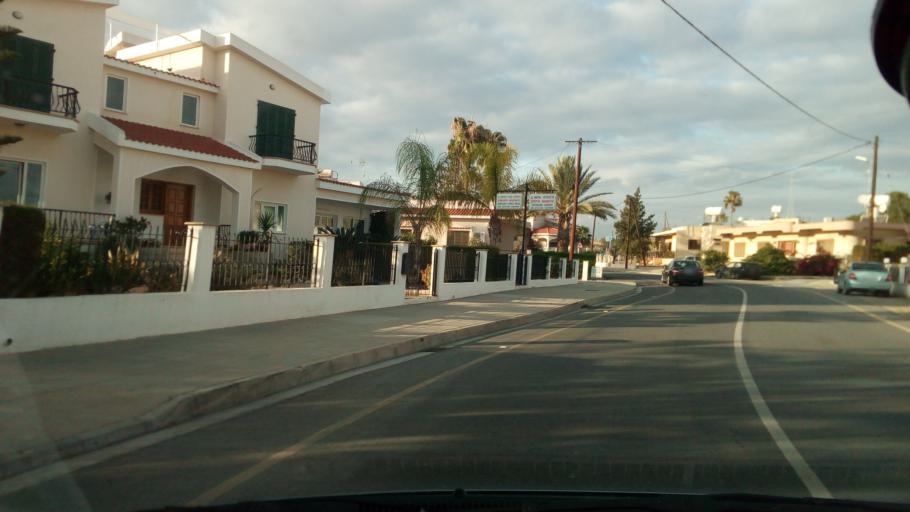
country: CY
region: Larnaka
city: Xylotymbou
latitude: 34.9983
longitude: 33.7629
